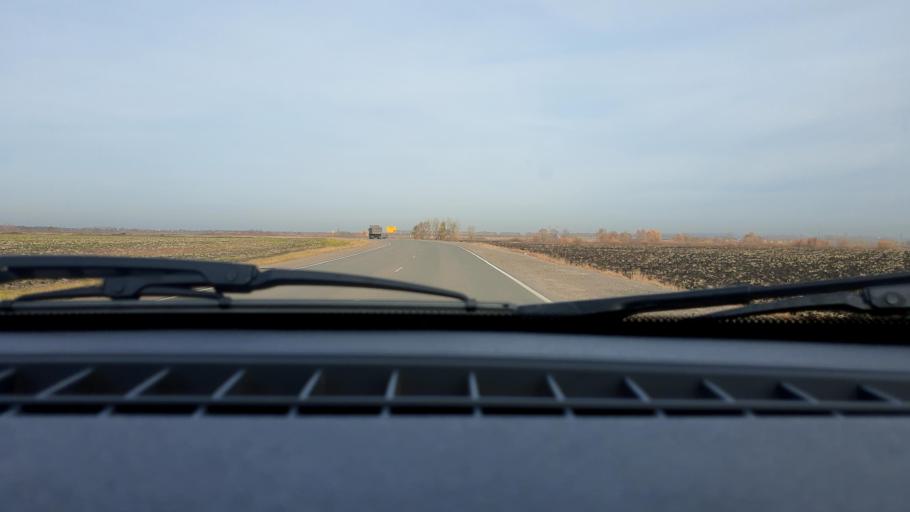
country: RU
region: Bashkortostan
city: Ufa
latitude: 54.8010
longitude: 55.9630
